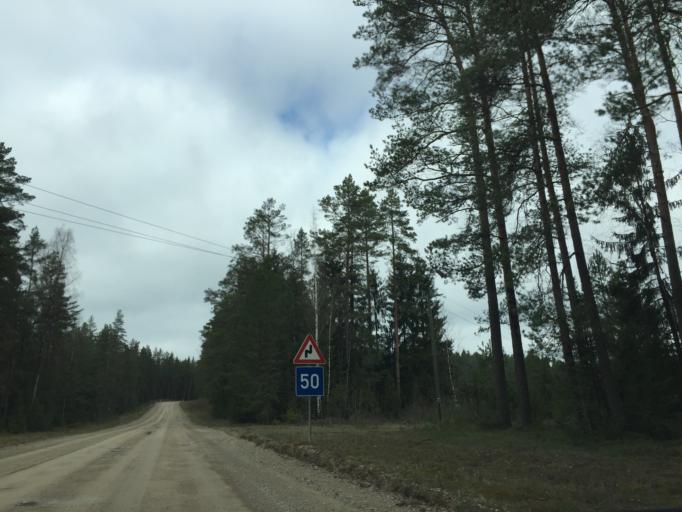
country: EE
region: Valgamaa
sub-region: Valga linn
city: Valga
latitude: 57.6601
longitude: 26.2035
